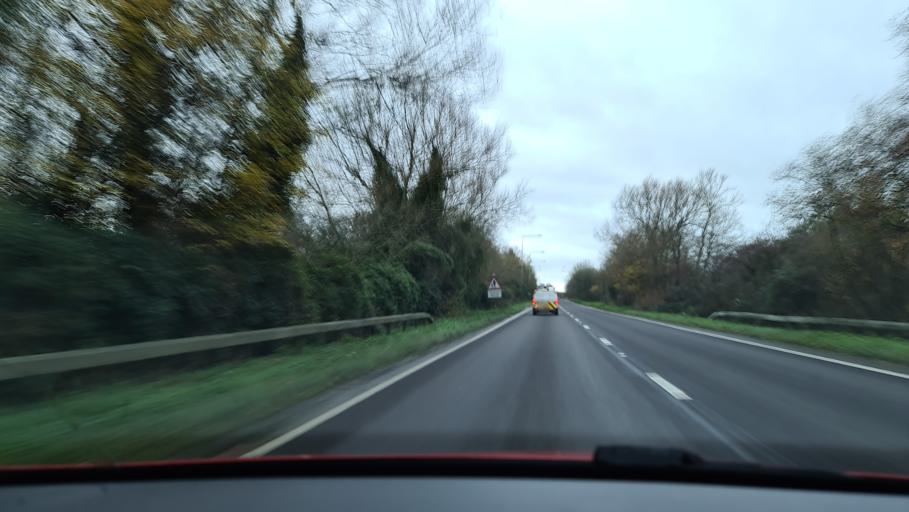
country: GB
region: England
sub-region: Oxfordshire
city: Bicester
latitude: 51.8750
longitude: -1.1878
